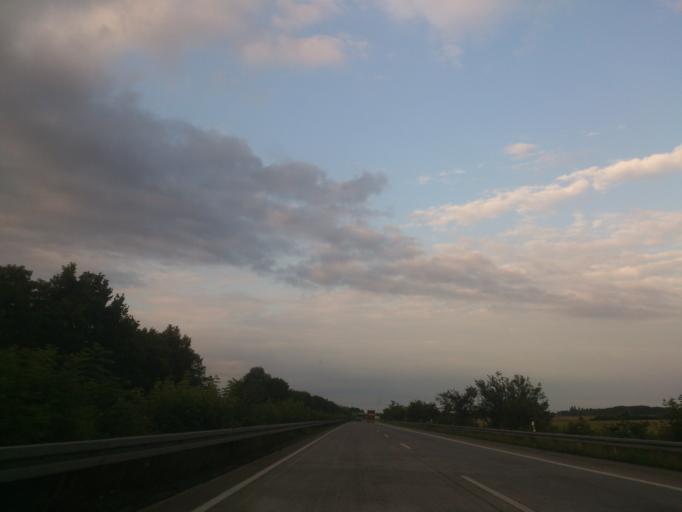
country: DE
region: North Rhine-Westphalia
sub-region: Regierungsbezirk Arnsberg
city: Soest
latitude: 51.5433
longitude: 8.0299
